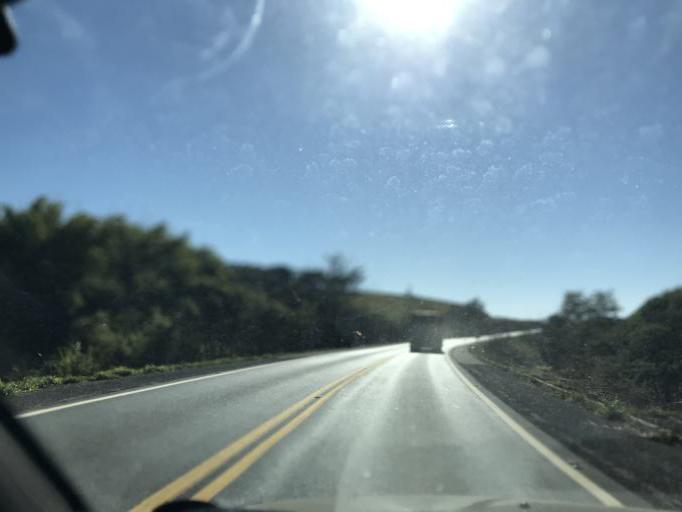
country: BR
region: Minas Gerais
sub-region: Bambui
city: Bambui
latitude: -19.8528
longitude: -45.9950
